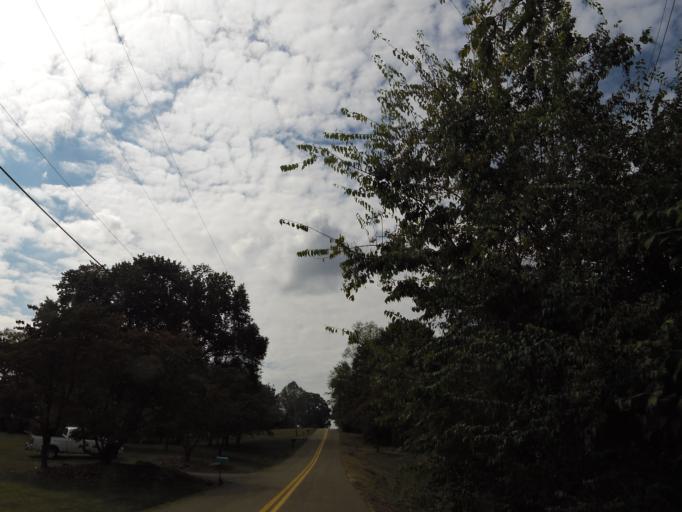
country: US
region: Tennessee
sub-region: Knox County
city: Knoxville
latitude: 36.0058
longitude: -83.8309
